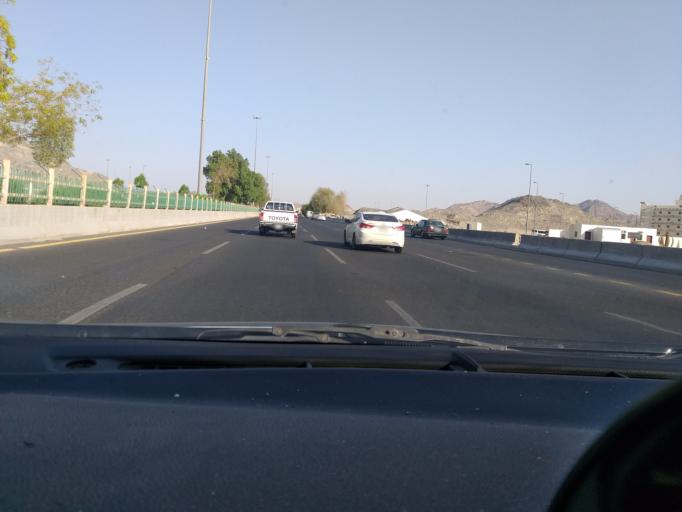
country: SA
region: Makkah
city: Mecca
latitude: 21.3702
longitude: 39.8840
